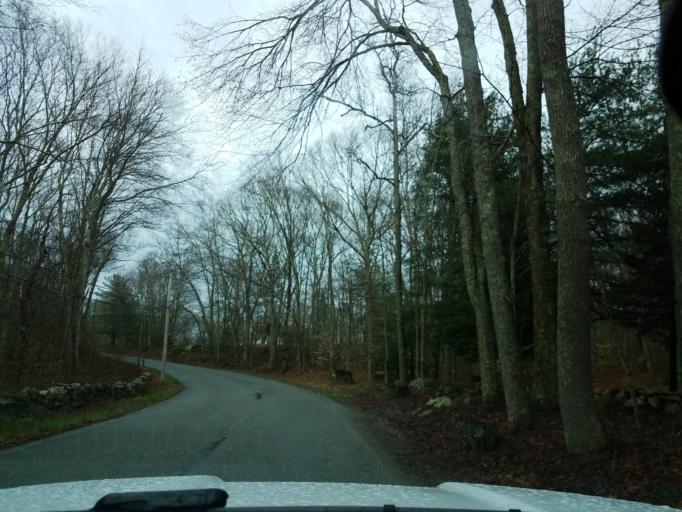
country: US
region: Rhode Island
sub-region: Washington County
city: Ashaway
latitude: 41.4467
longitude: -71.8226
